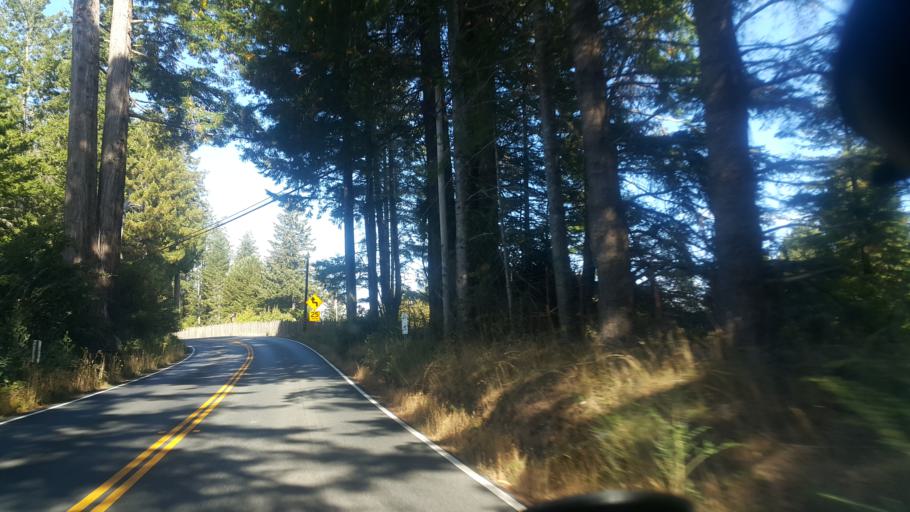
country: US
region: California
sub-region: Mendocino County
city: Fort Bragg
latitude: 39.4073
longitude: -123.7272
